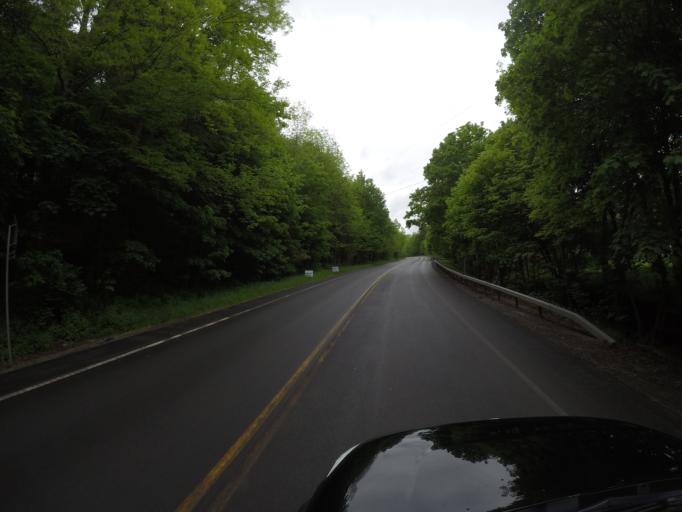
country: US
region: New York
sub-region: Delaware County
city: Delhi
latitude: 42.1925
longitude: -74.7884
